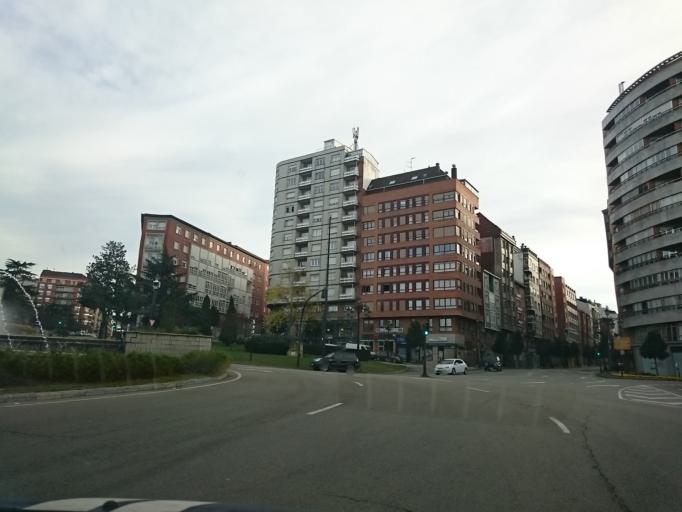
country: ES
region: Asturias
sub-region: Province of Asturias
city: Oviedo
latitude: 43.3563
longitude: -5.8586
